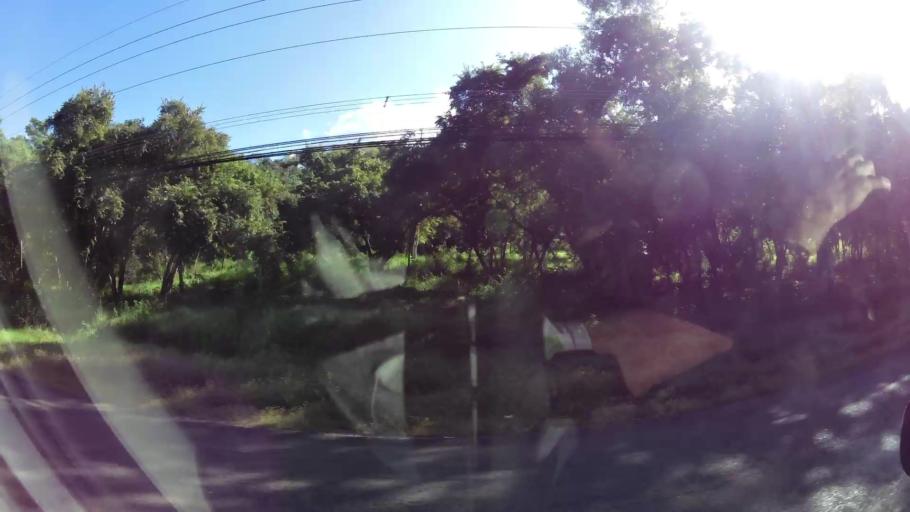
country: CR
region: Guanacaste
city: Sardinal
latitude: 10.5867
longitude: -85.6516
